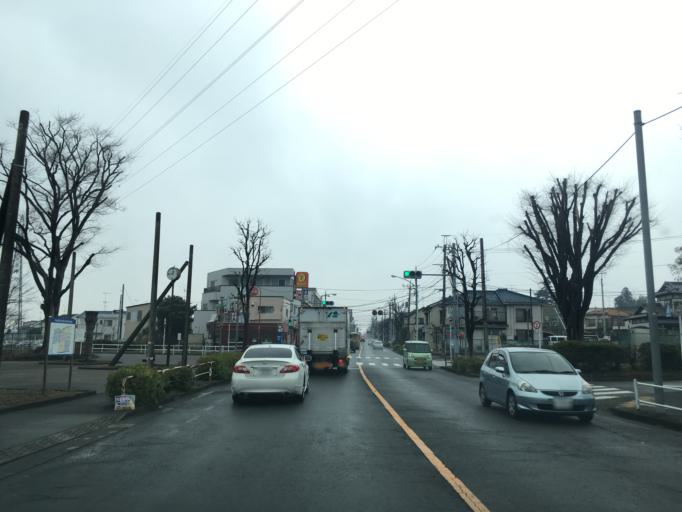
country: JP
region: Tokyo
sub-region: Machida-shi
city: Machida
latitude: 35.5617
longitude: 139.4221
